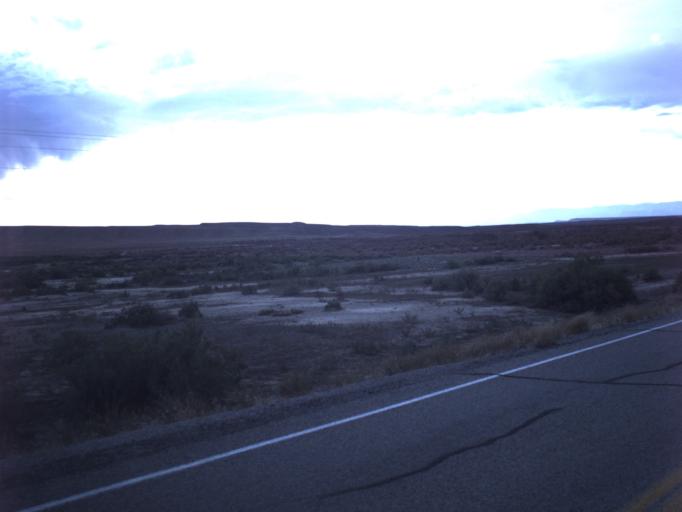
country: US
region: Utah
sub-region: Grand County
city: Moab
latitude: 38.8716
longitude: -109.3028
